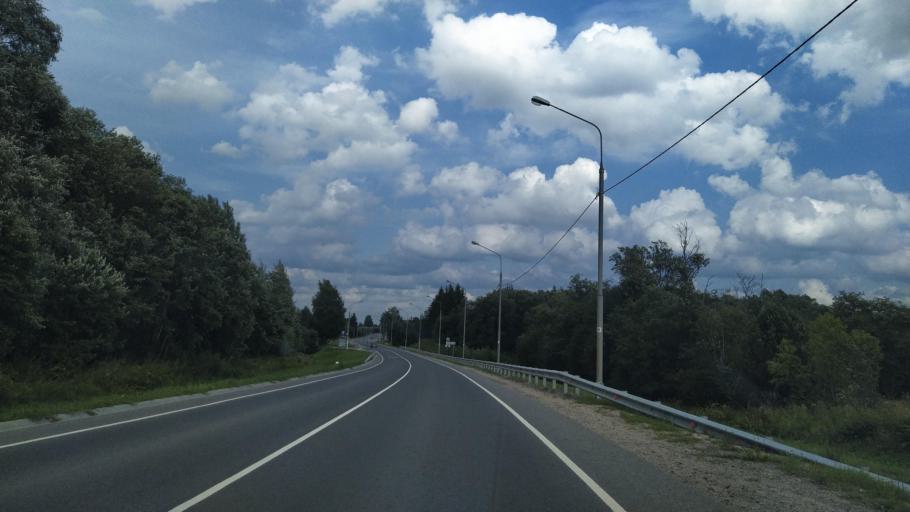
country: RU
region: Pskov
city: Dno
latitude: 58.0590
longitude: 29.9753
